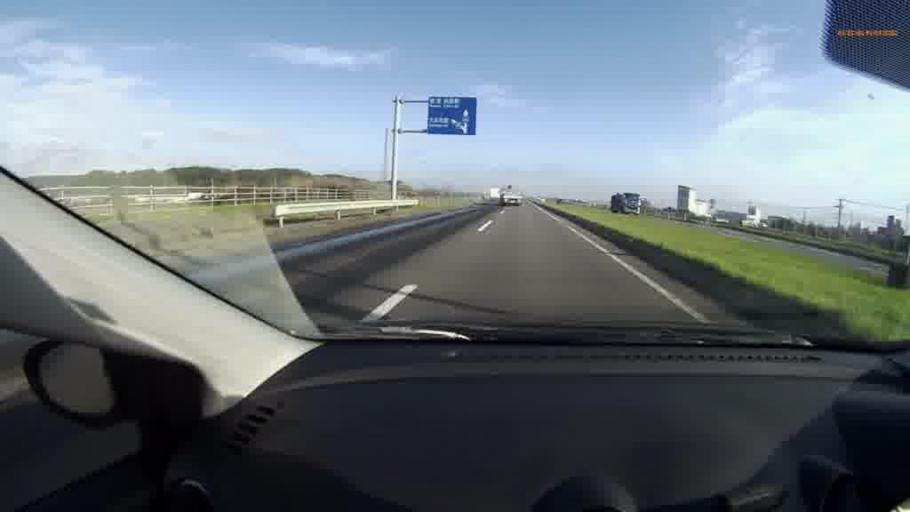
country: JP
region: Hokkaido
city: Kushiro
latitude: 43.0051
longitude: 144.2547
